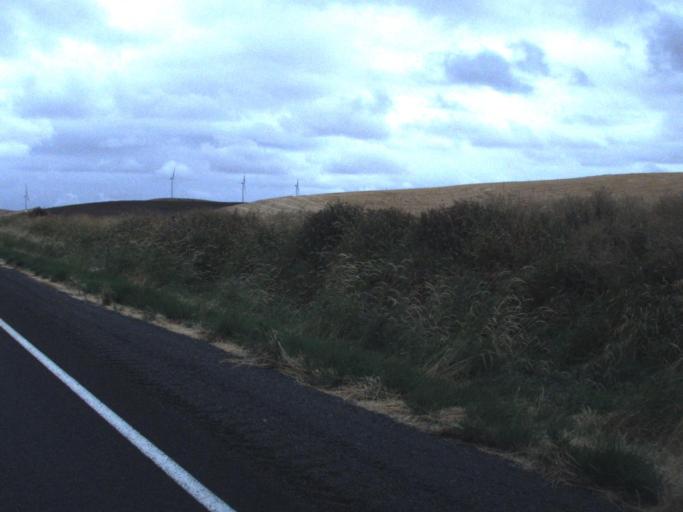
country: US
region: Washington
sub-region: Whitman County
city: Colfax
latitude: 47.1730
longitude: -117.2918
